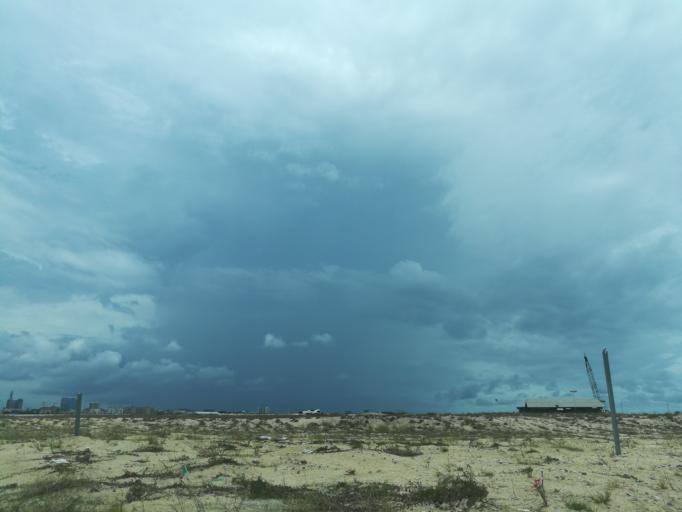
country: NG
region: Lagos
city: Ikoyi
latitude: 6.4133
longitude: 3.4256
